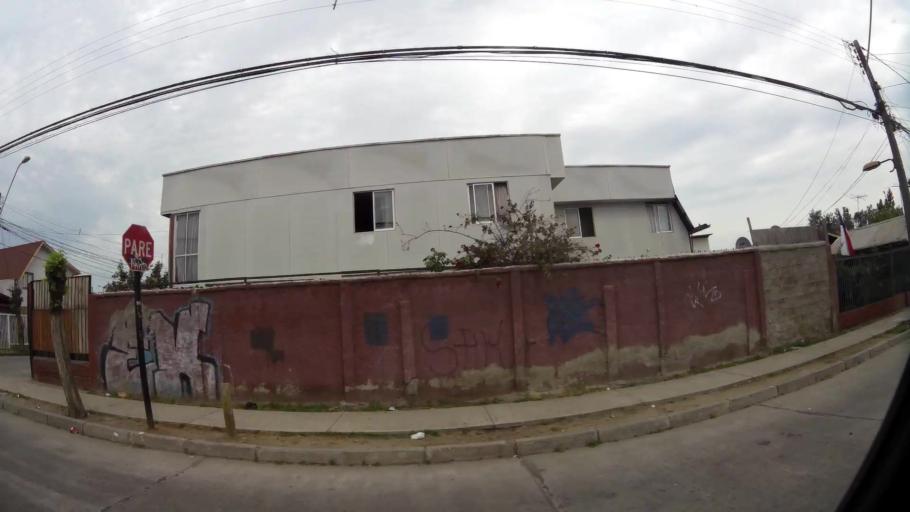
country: CL
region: Santiago Metropolitan
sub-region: Provincia de Santiago
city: Lo Prado
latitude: -33.5009
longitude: -70.7735
